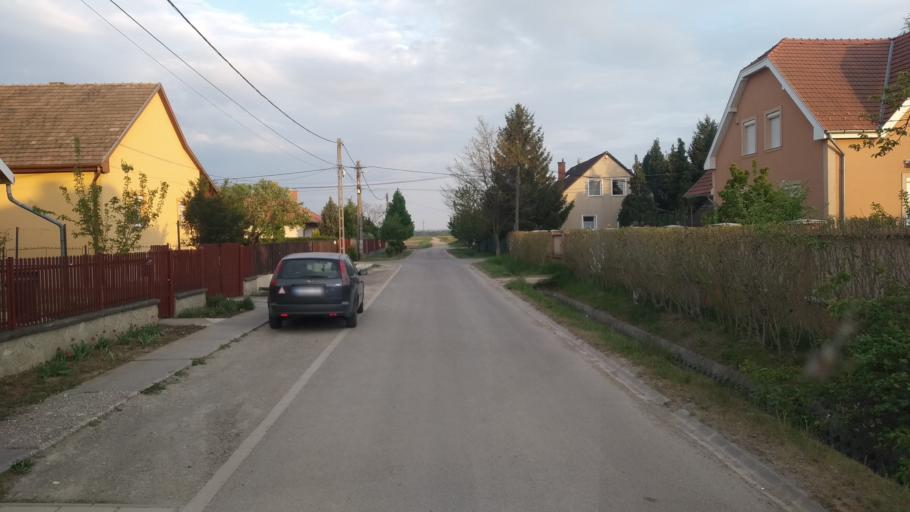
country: HU
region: Pest
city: Tahitotfalu
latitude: 47.7514
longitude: 19.1005
